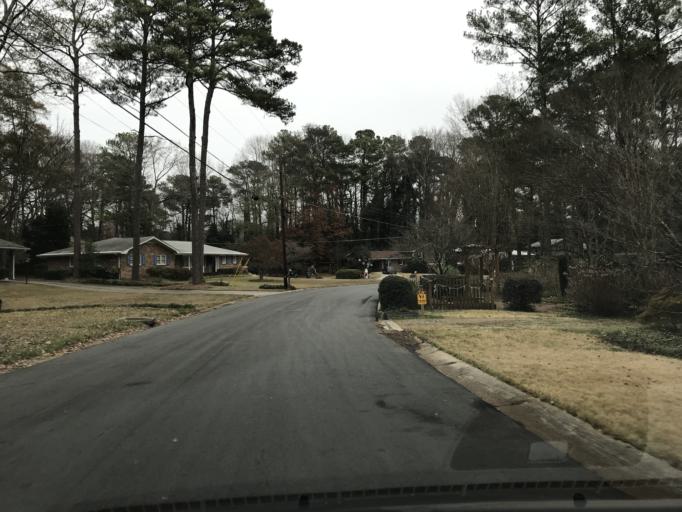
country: US
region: Georgia
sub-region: DeKalb County
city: Clarkston
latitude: 33.8239
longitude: -84.2549
